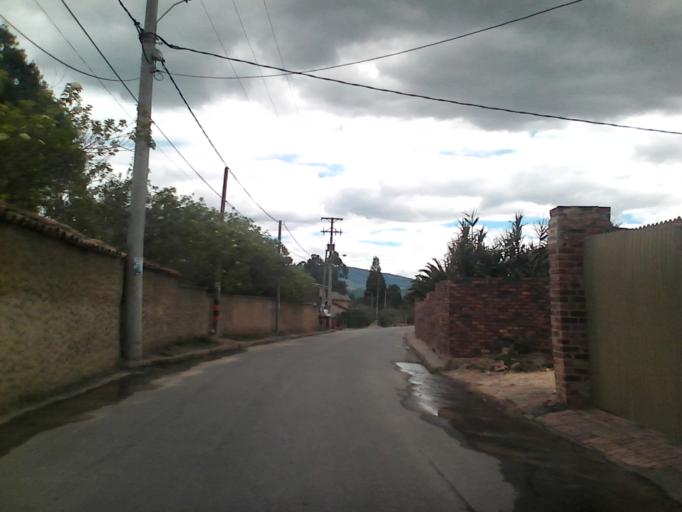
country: CO
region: Boyaca
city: Duitama
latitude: 5.8195
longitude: -73.0708
